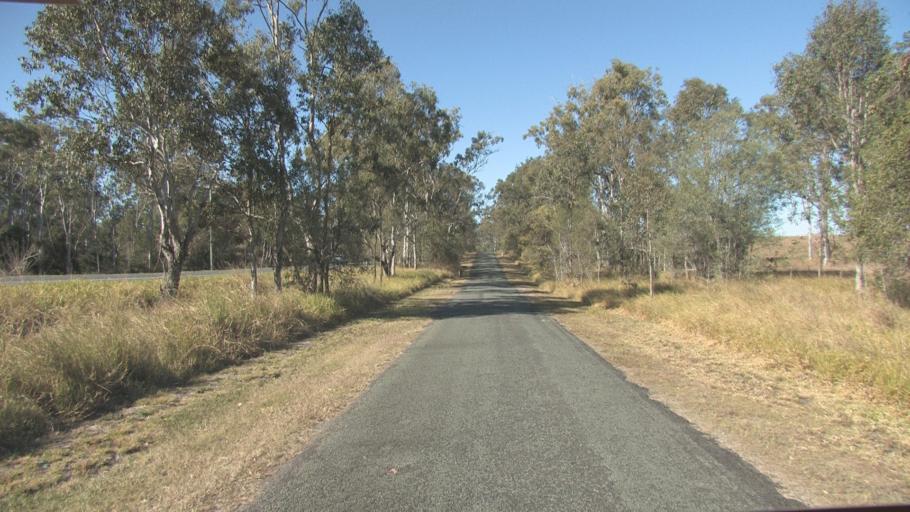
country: AU
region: Queensland
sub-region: Logan
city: North Maclean
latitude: -27.8000
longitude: 153.0224
